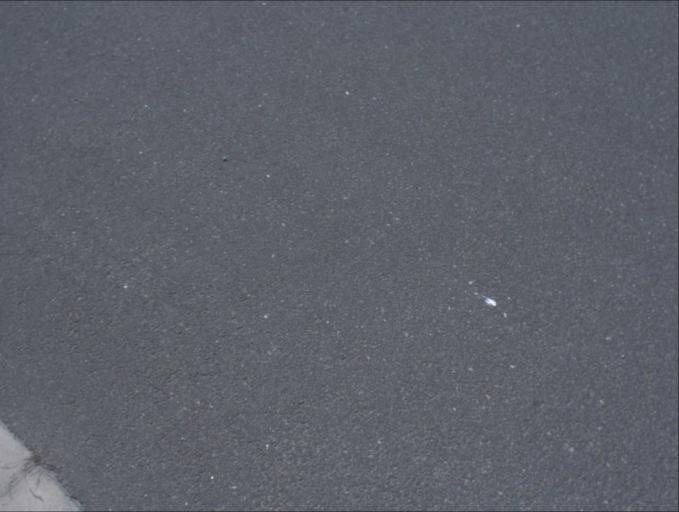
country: AU
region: Queensland
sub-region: Logan
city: Woodridge
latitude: -27.6484
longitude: 153.0928
